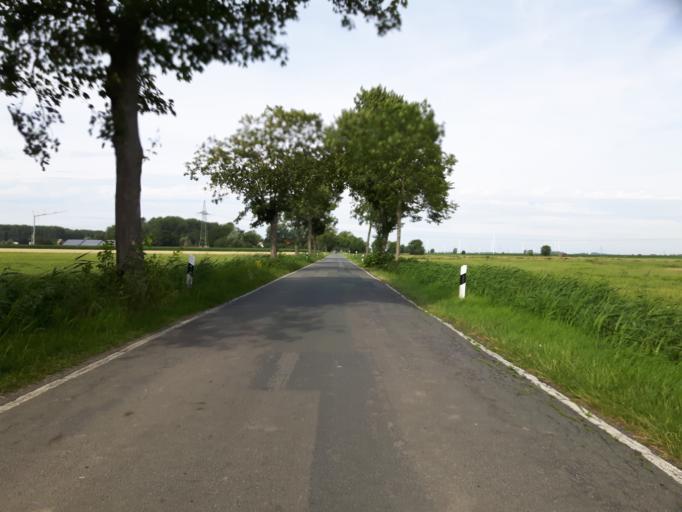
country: DE
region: Lower Saxony
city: Elsfleth
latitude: 53.2572
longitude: 8.4556
